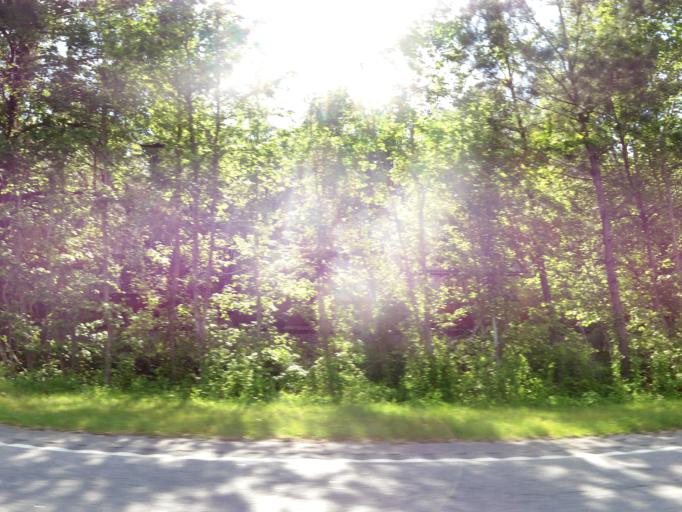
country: US
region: South Carolina
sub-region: Allendale County
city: Fairfax
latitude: 32.9117
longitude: -81.2376
